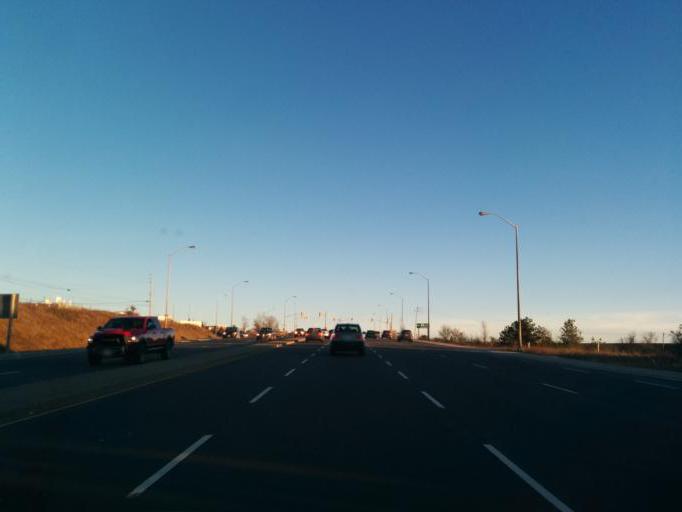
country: CA
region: Ontario
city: Orangeville
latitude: 43.9202
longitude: -80.0793
